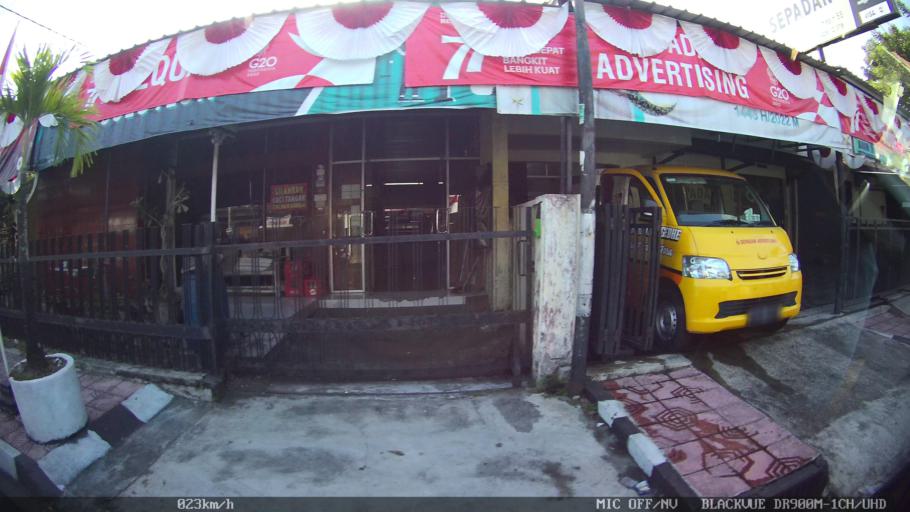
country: ID
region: Daerah Istimewa Yogyakarta
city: Yogyakarta
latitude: -7.8076
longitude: 110.3669
